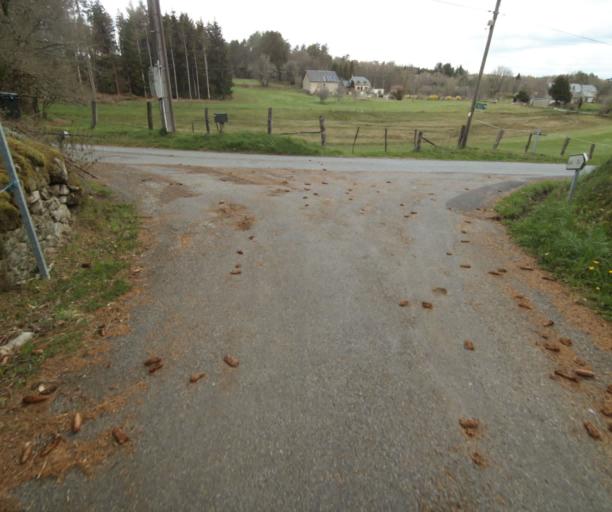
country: FR
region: Limousin
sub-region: Departement de la Correze
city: Correze
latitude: 45.2682
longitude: 1.9576
